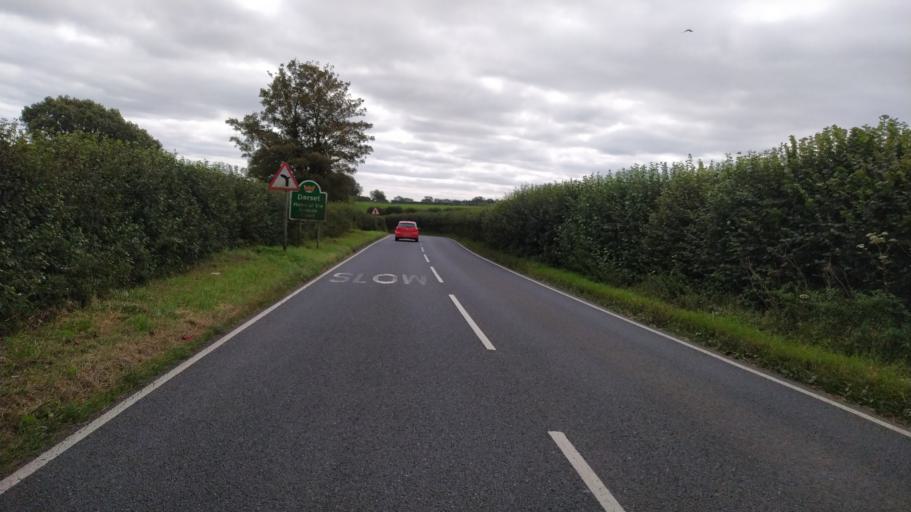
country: GB
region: England
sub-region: Somerset
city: Wincanton
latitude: 51.0611
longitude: -2.3491
